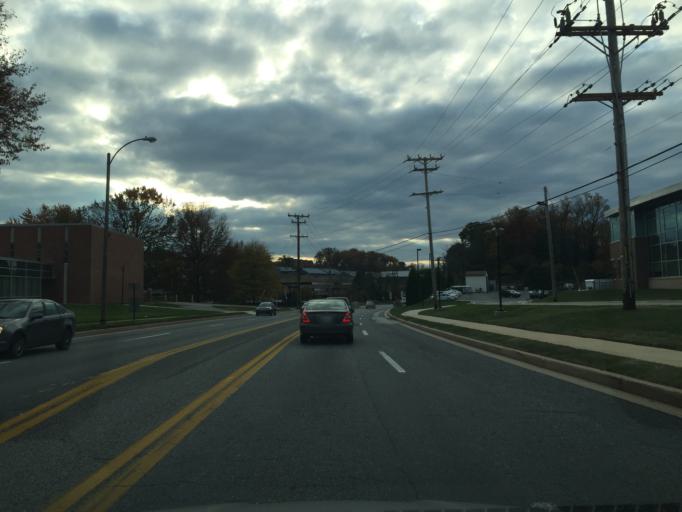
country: US
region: Maryland
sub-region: Baltimore County
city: Towson
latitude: 39.3960
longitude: -76.6123
